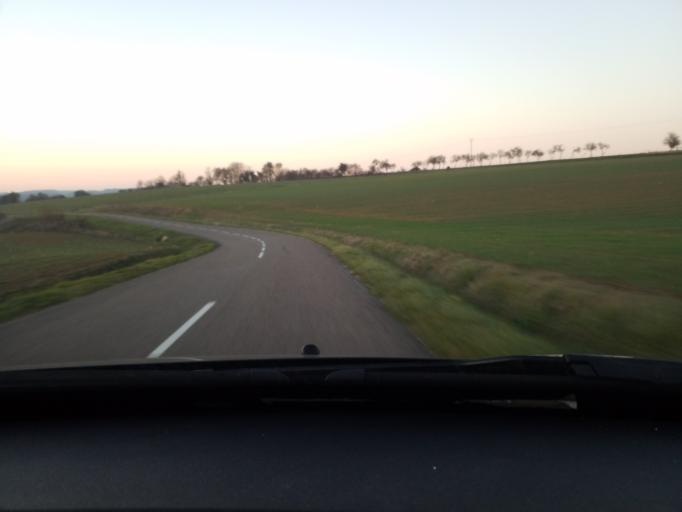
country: FR
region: Franche-Comte
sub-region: Departement de la Haute-Saone
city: Faverney
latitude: 47.8821
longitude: 6.1445
